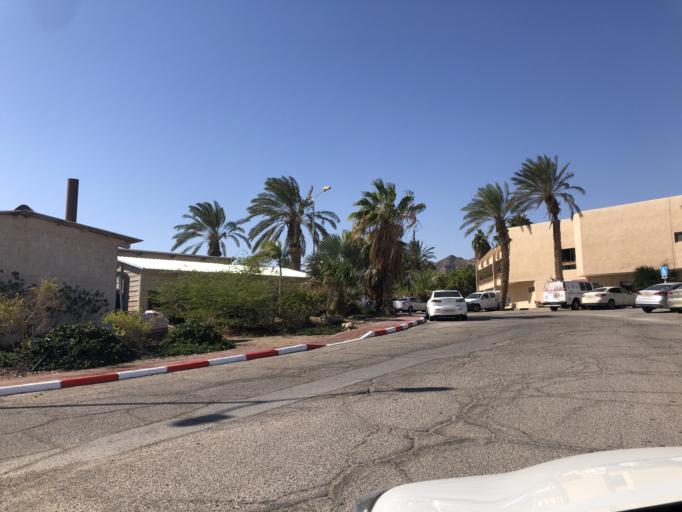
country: IL
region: Southern District
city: Eilat
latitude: 29.5815
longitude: 34.9642
